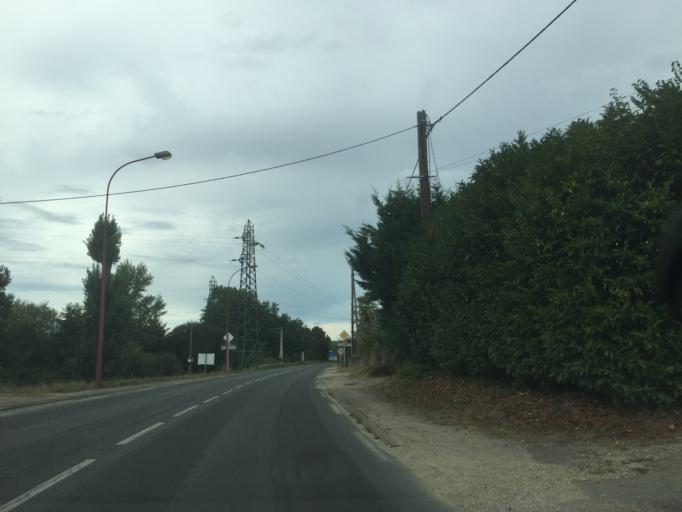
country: FR
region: Aquitaine
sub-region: Departement du Lot-et-Garonne
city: Monsempron-Libos
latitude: 44.4962
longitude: 0.9452
